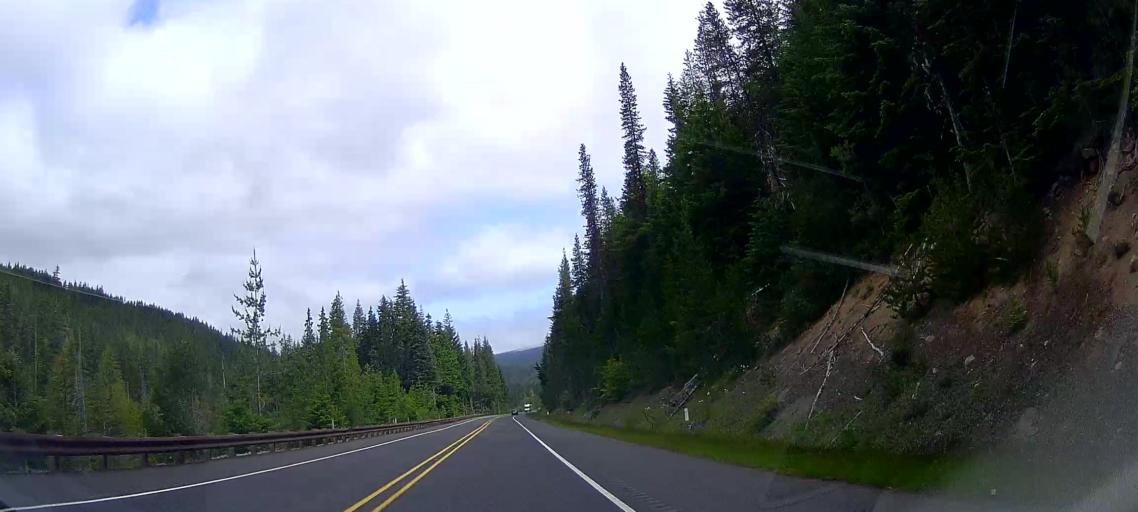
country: US
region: Oregon
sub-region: Clackamas County
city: Mount Hood Village
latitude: 45.2681
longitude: -121.7179
